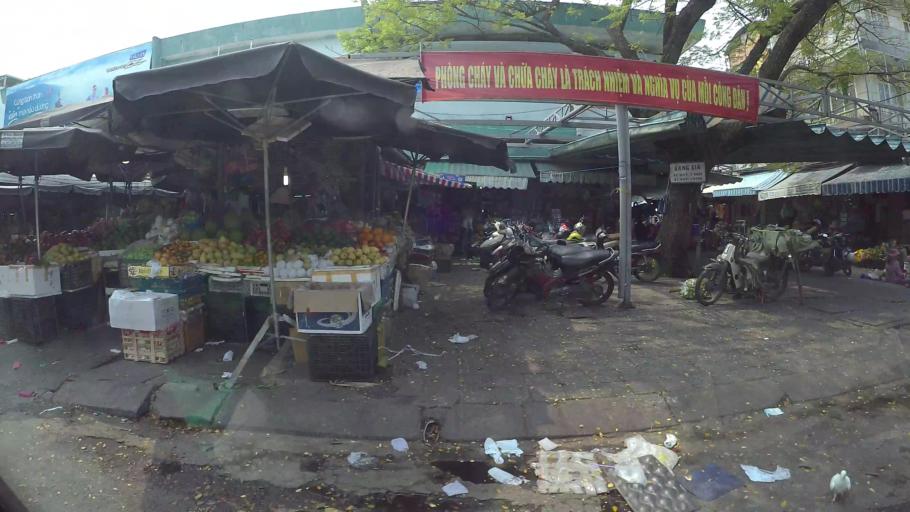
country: VN
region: Da Nang
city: Da Nang
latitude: 16.0508
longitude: 108.2180
